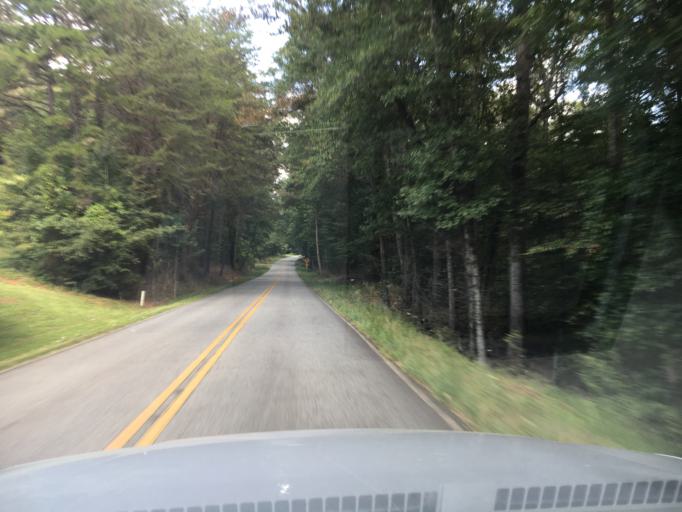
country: US
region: South Carolina
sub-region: Spartanburg County
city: Wellford
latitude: 34.8958
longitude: -82.0606
